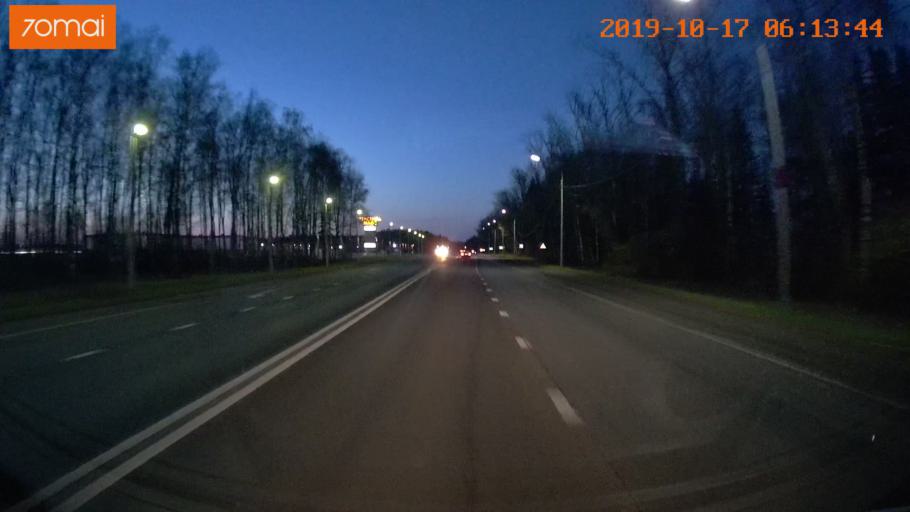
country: RU
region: Ivanovo
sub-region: Gorod Ivanovo
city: Ivanovo
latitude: 56.8947
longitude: 40.9376
